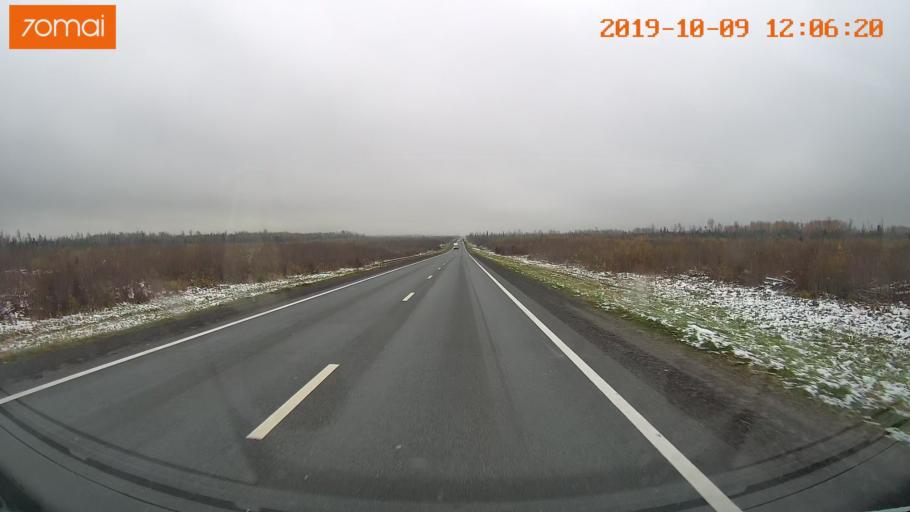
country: RU
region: Jaroslavl
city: Prechistoye
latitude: 58.6160
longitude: 40.3345
